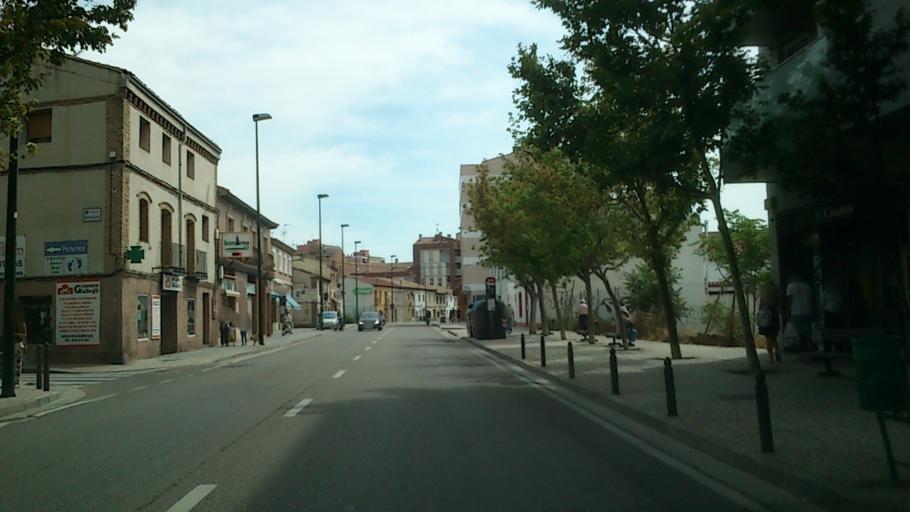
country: ES
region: Aragon
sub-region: Provincia de Zaragoza
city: Zaragoza
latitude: 41.6668
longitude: -0.8296
